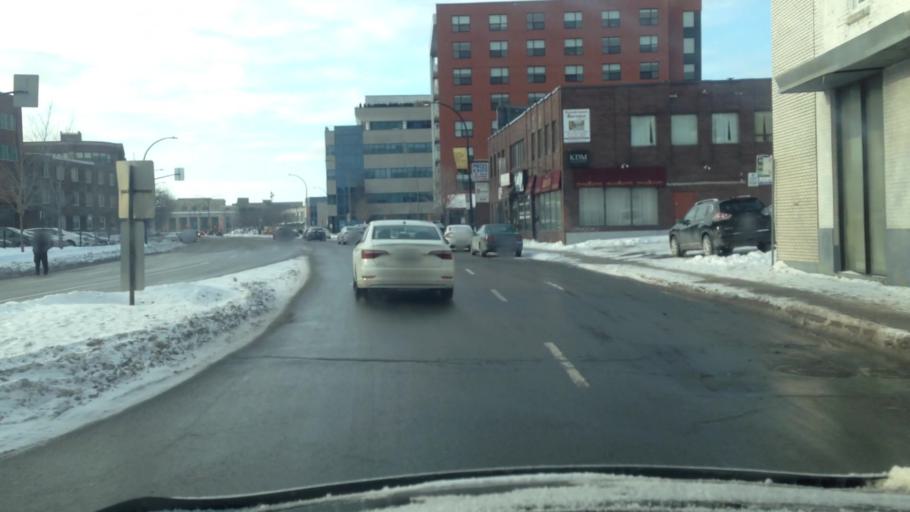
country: CA
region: Quebec
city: Mont-Royal
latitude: 45.5292
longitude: -73.6179
